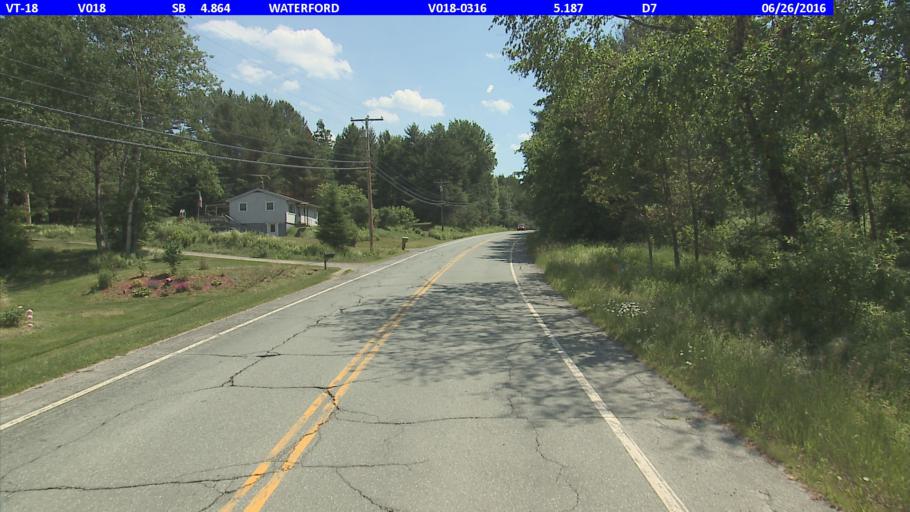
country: US
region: Vermont
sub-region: Caledonia County
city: Saint Johnsbury
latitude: 44.4017
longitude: -71.9229
